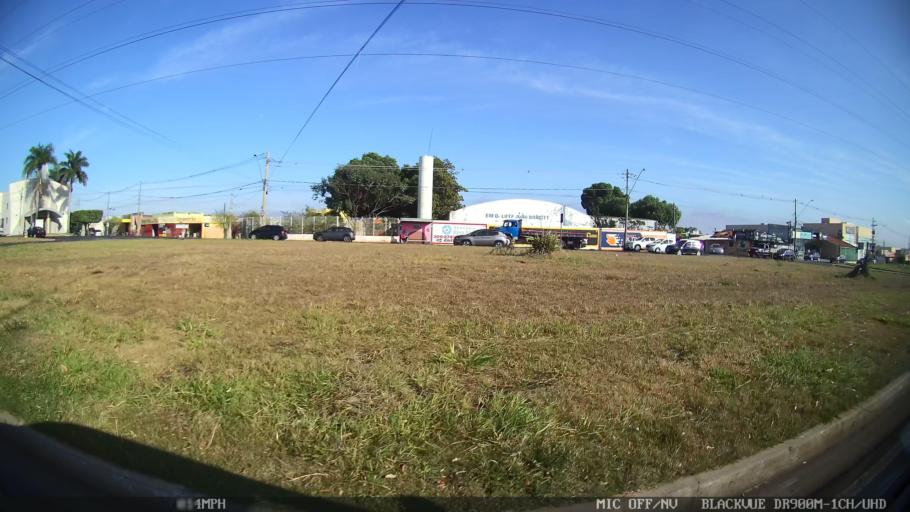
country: BR
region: Sao Paulo
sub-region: Sao Jose Do Rio Preto
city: Sao Jose do Rio Preto
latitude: -20.7903
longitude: -49.3441
